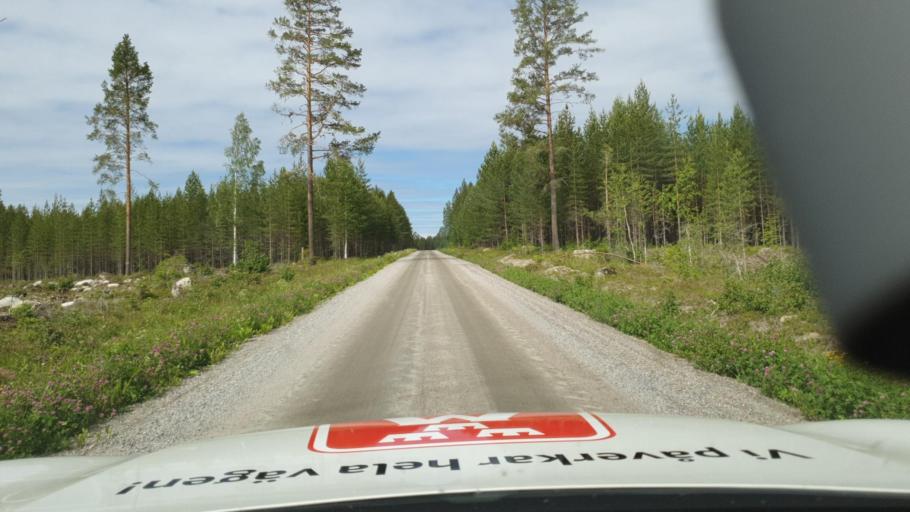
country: SE
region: Vaesterbotten
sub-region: Skelleftea Kommun
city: Burtraesk
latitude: 64.6149
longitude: 20.5861
